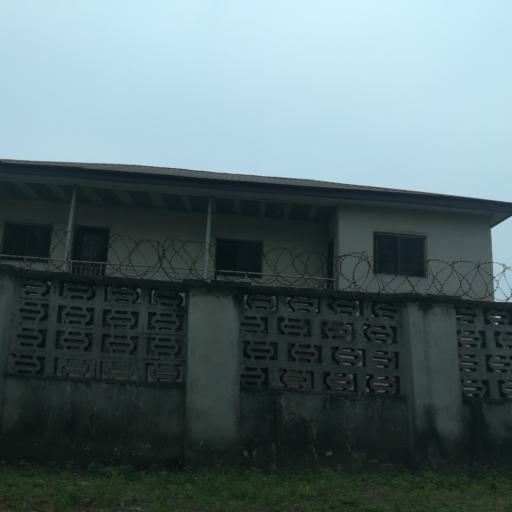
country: NG
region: Rivers
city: Port Harcourt
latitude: 4.7954
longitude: 7.0070
